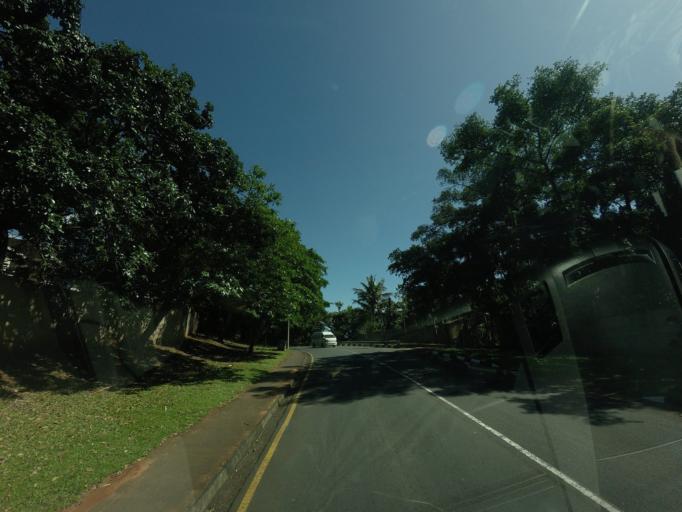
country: ZA
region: KwaZulu-Natal
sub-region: iLembe District Municipality
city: Ballitoville
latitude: -29.5362
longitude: 31.2131
